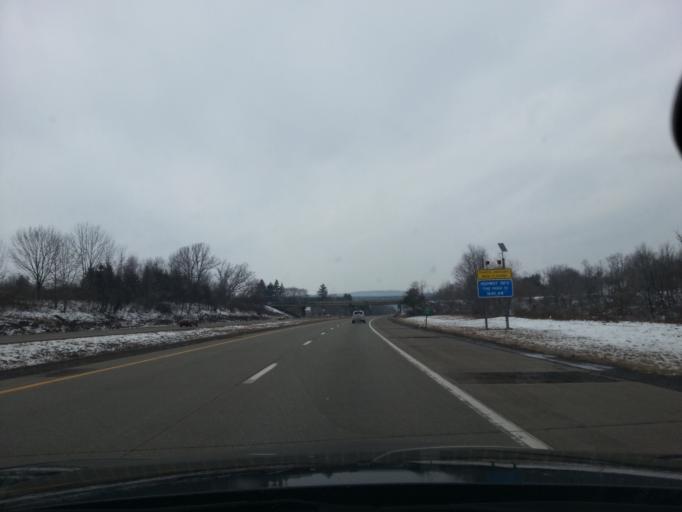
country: US
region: Pennsylvania
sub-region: Luzerne County
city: Harleigh
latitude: 41.0094
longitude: -76.0089
